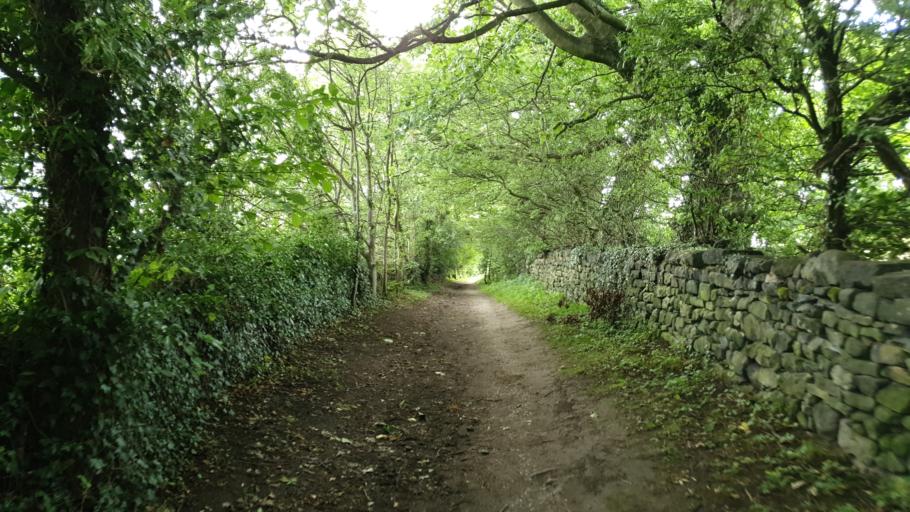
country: GB
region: England
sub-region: City and Borough of Leeds
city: Guiseley
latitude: 53.8806
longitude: -1.7139
